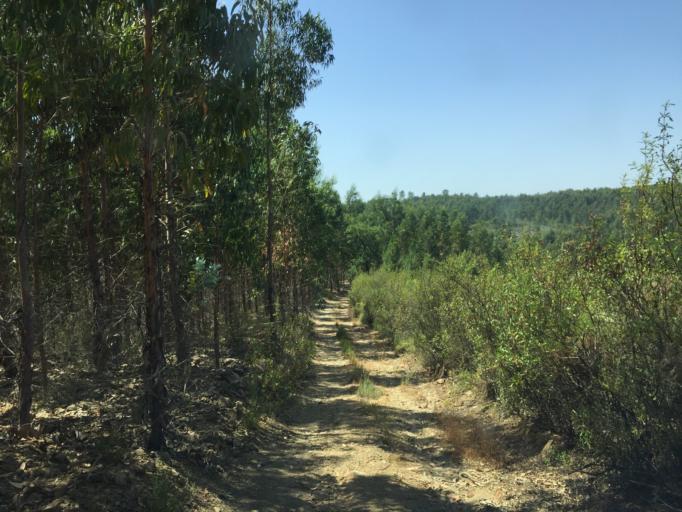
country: PT
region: Santarem
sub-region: Ferreira do Zezere
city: Ferreira do Zezere
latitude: 39.6520
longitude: -8.3166
